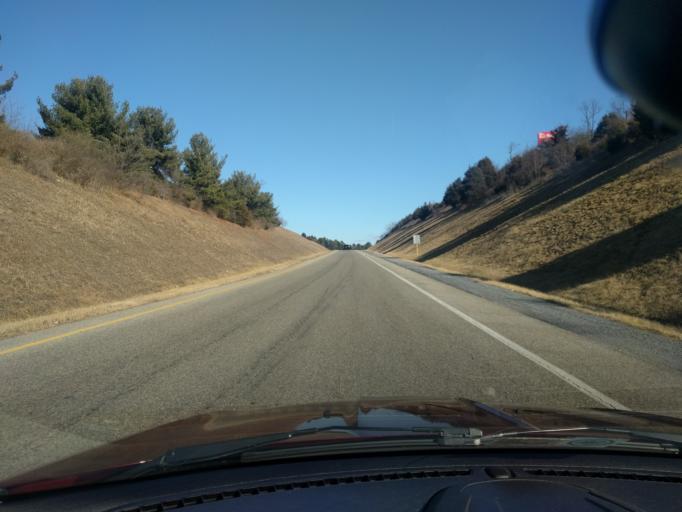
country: US
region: Virginia
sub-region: Augusta County
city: Jolivue
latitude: 38.1270
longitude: -79.0334
